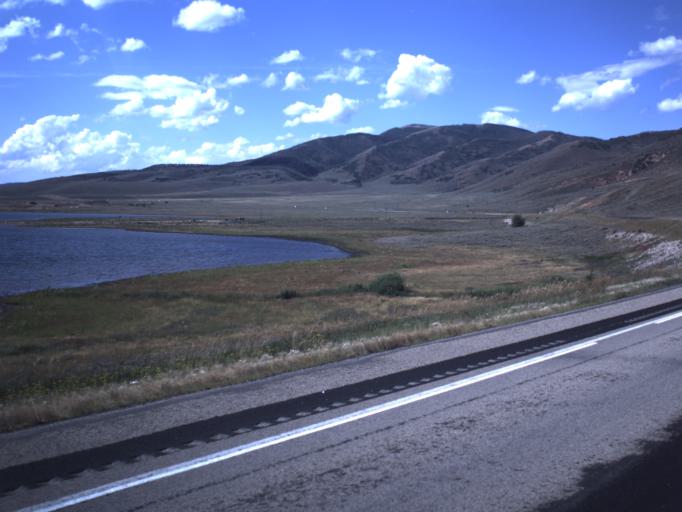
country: US
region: Utah
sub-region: Wasatch County
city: Heber
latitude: 40.2102
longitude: -111.1026
